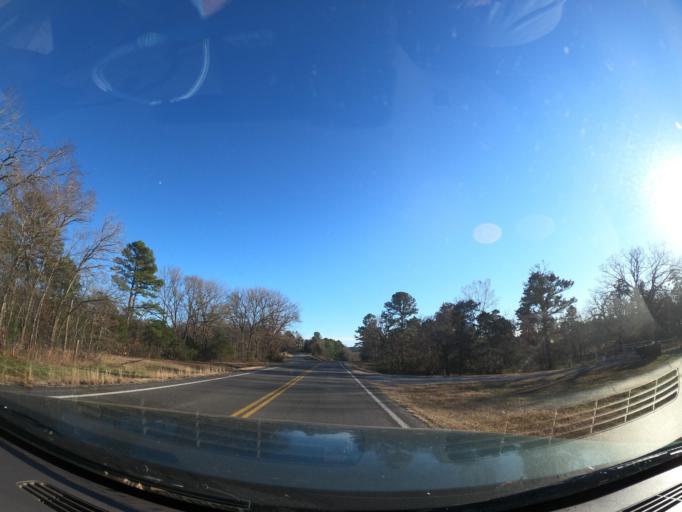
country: US
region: Oklahoma
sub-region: Latimer County
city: Wilburton
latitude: 34.9528
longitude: -95.3426
